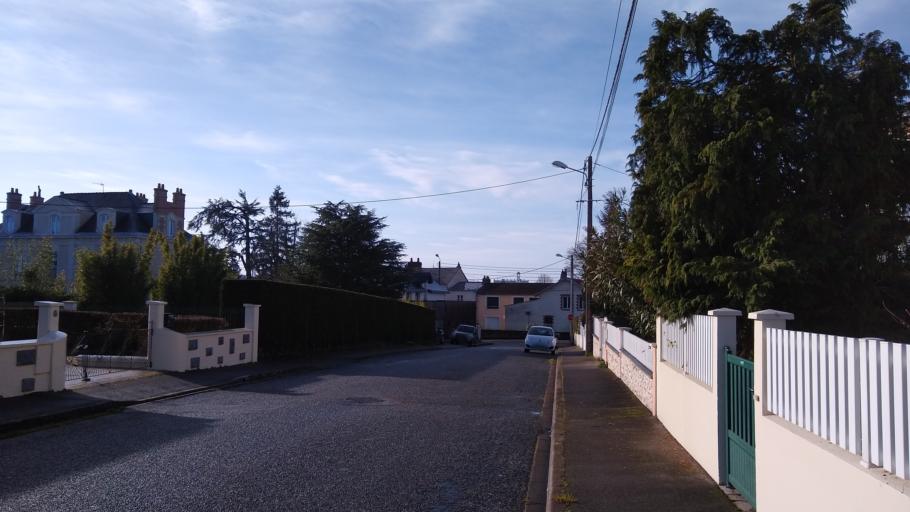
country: FR
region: Pays de la Loire
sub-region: Departement de la Loire-Atlantique
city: Saint-Sebastien-sur-Loire
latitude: 47.1963
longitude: -1.5174
